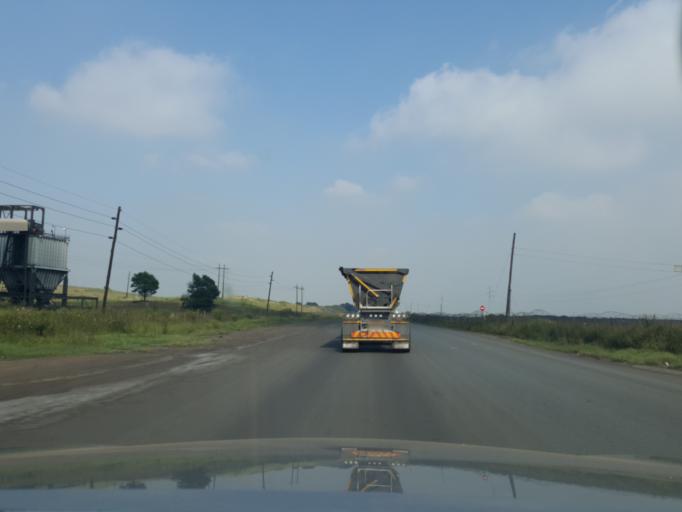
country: ZA
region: Mpumalanga
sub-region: Nkangala District Municipality
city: Witbank
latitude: -26.0144
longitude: 29.3486
